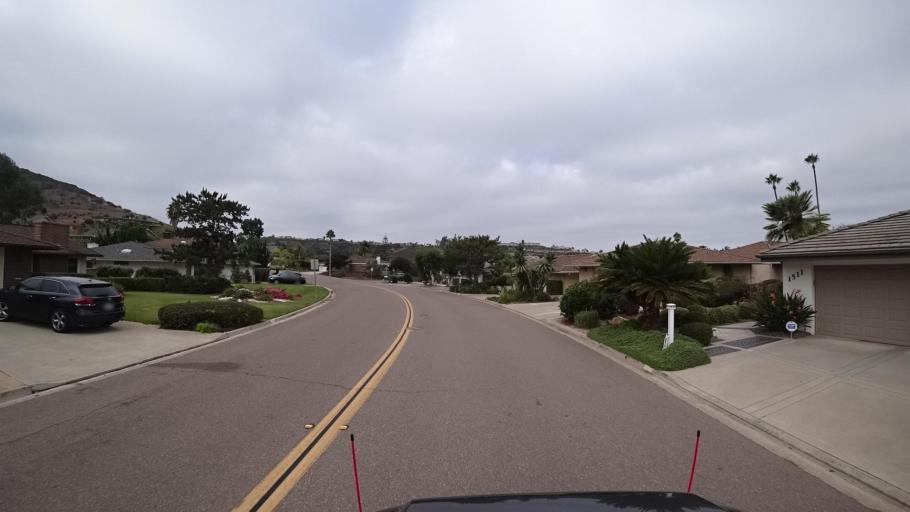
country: US
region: California
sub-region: San Diego County
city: Lake San Marcos
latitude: 33.1194
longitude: -117.2046
